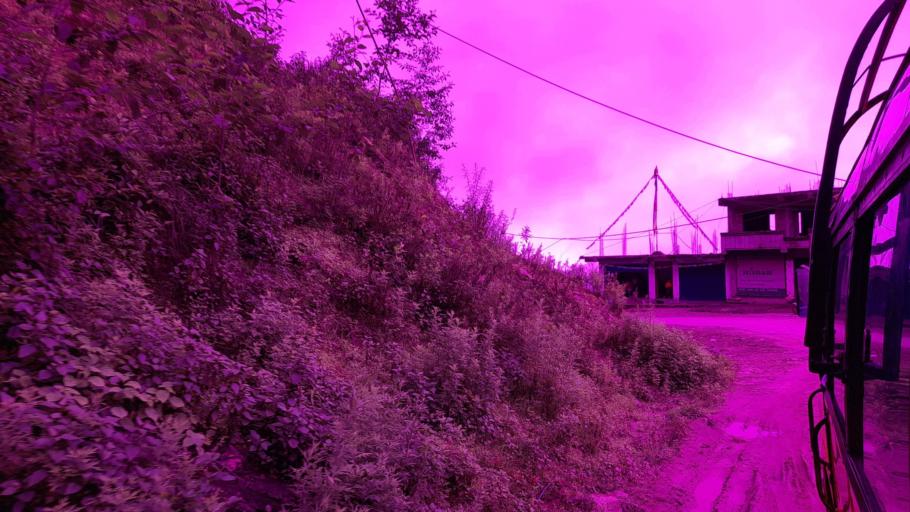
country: NP
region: Central Region
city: Kirtipur
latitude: 27.8260
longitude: 85.2089
